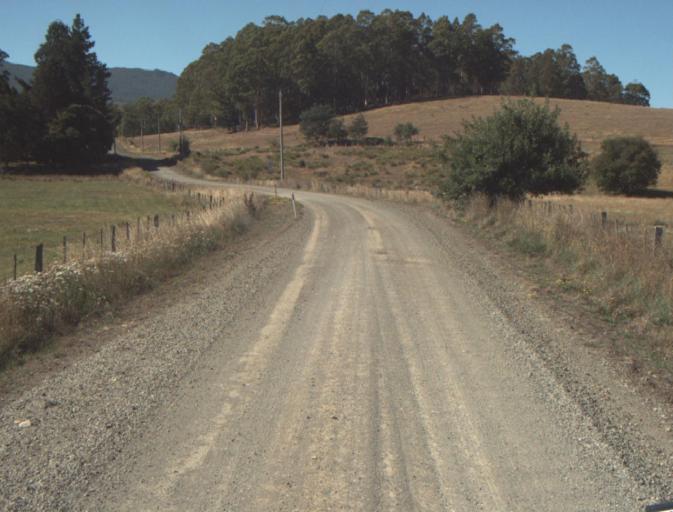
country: AU
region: Tasmania
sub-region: Launceston
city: Newstead
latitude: -41.3306
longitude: 147.3444
